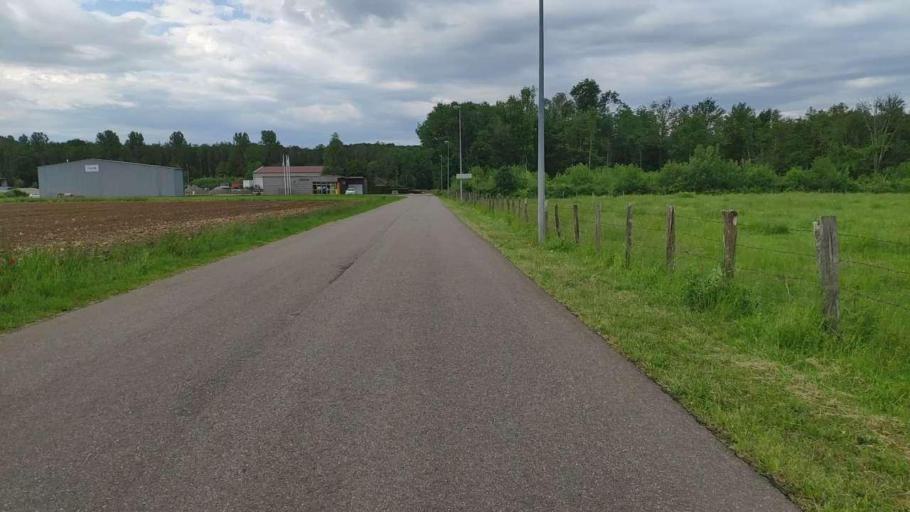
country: FR
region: Franche-Comte
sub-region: Departement du Jura
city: Perrigny
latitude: 46.7596
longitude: 5.5969
